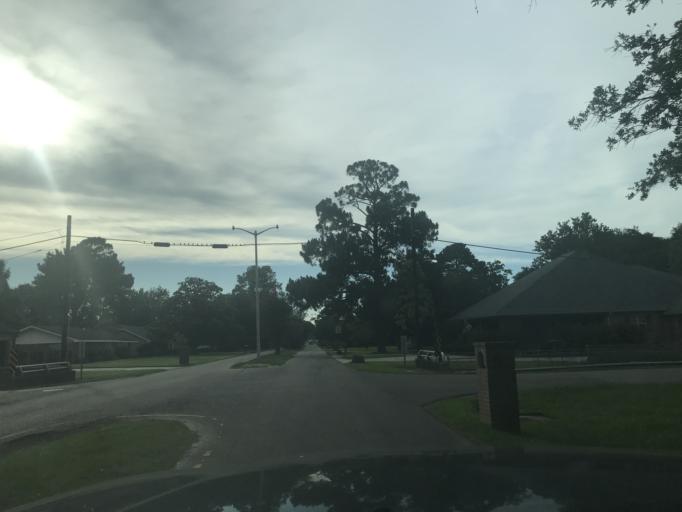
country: US
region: Louisiana
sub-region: Lafayette Parish
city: Lafayette
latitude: 30.1937
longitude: -92.0537
